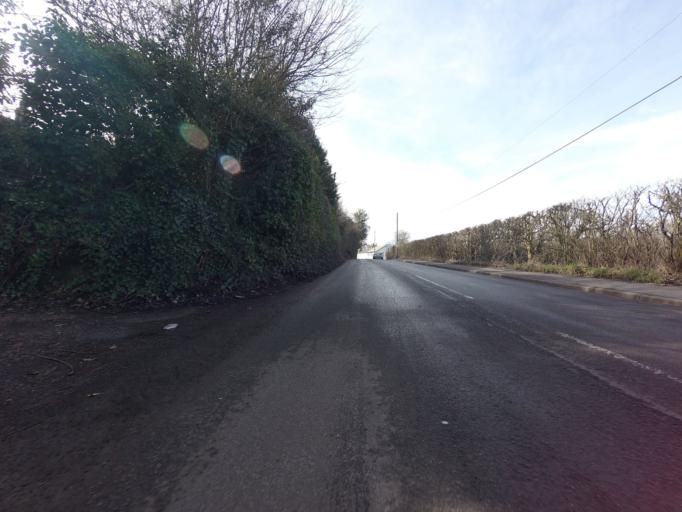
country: GB
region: England
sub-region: Kent
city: Swanley
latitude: 51.3838
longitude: 0.1665
